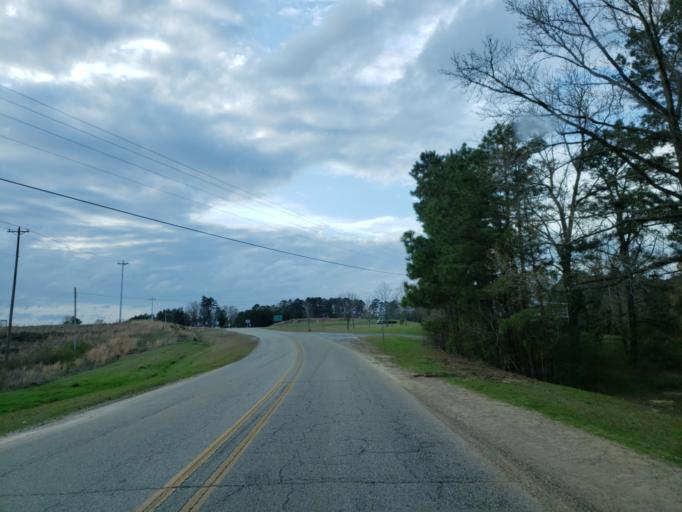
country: US
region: Mississippi
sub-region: Clarke County
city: Stonewall
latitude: 32.2109
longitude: -88.6954
